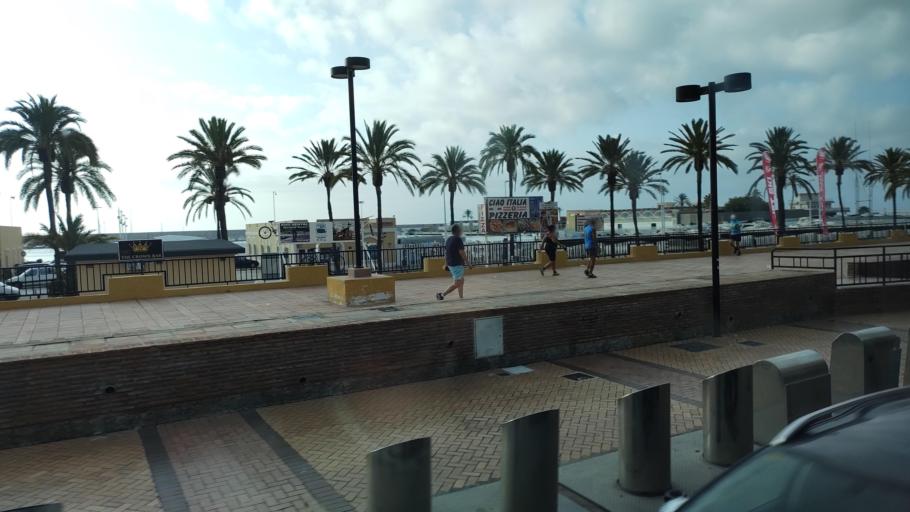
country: ES
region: Andalusia
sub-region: Provincia de Malaga
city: Fuengirola
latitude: 36.5413
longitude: -4.6196
